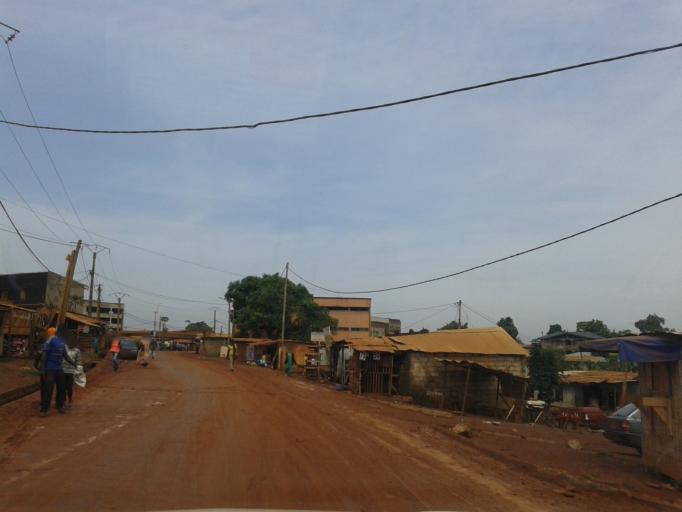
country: CM
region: Centre
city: Yaounde
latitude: 3.9244
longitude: 11.5174
